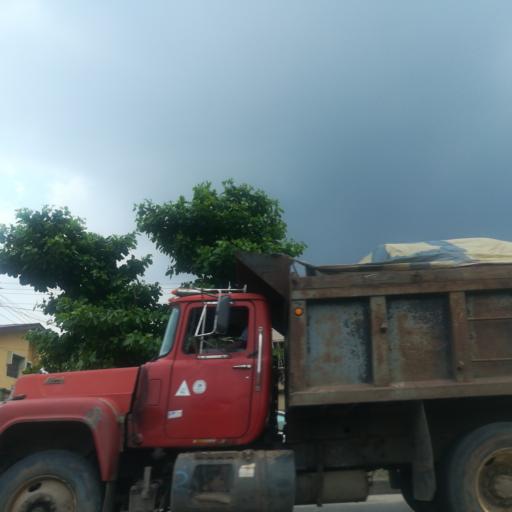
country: NG
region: Lagos
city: Ojota
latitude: 6.5803
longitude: 3.3861
